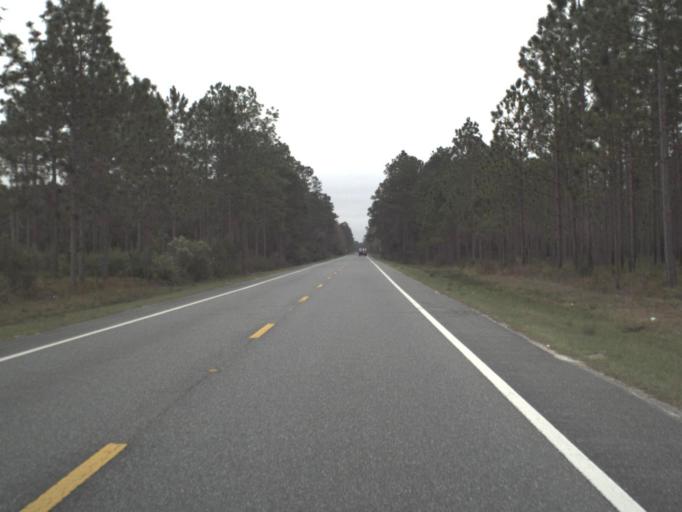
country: US
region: Florida
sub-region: Gulf County
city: Wewahitchka
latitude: 29.9964
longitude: -84.9771
